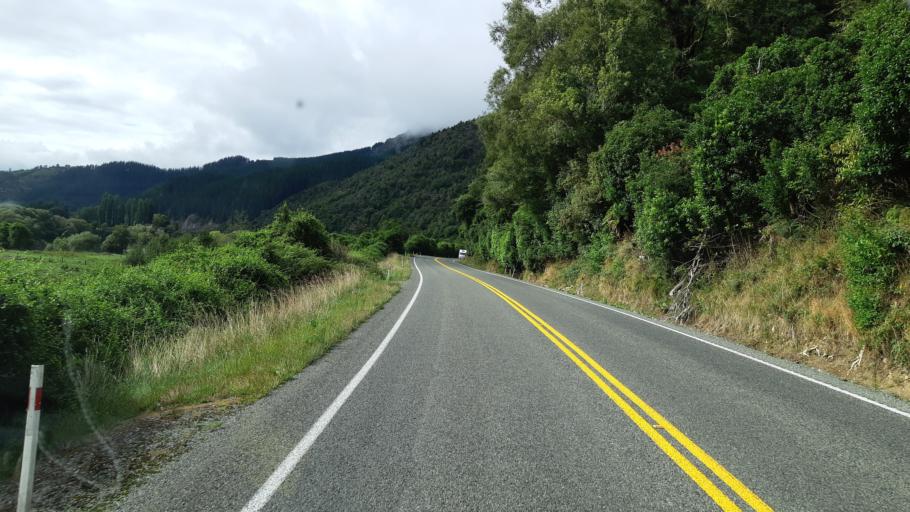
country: NZ
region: West Coast
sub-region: Buller District
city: Westport
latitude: -41.7708
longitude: 172.2368
